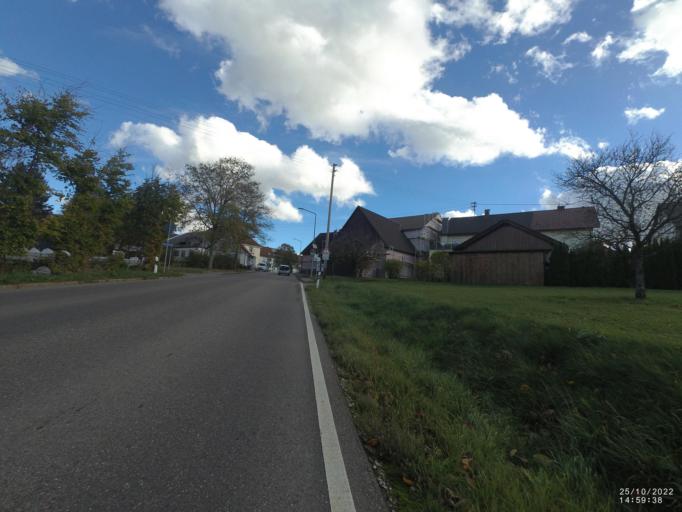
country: DE
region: Baden-Wuerttemberg
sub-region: Regierungsbezirk Stuttgart
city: Bohmenkirch
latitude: 48.6642
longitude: 9.9087
